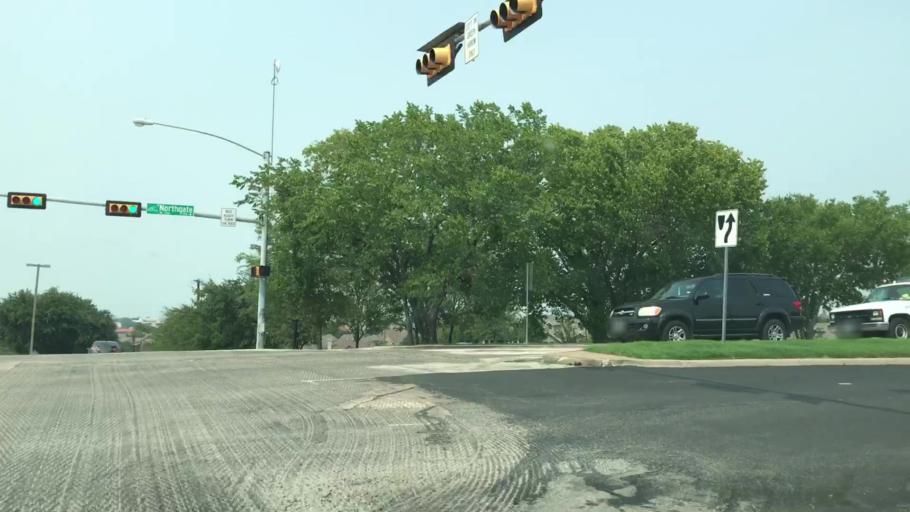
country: US
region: Texas
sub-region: Dallas County
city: Irving
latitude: 32.8553
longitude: -96.9751
